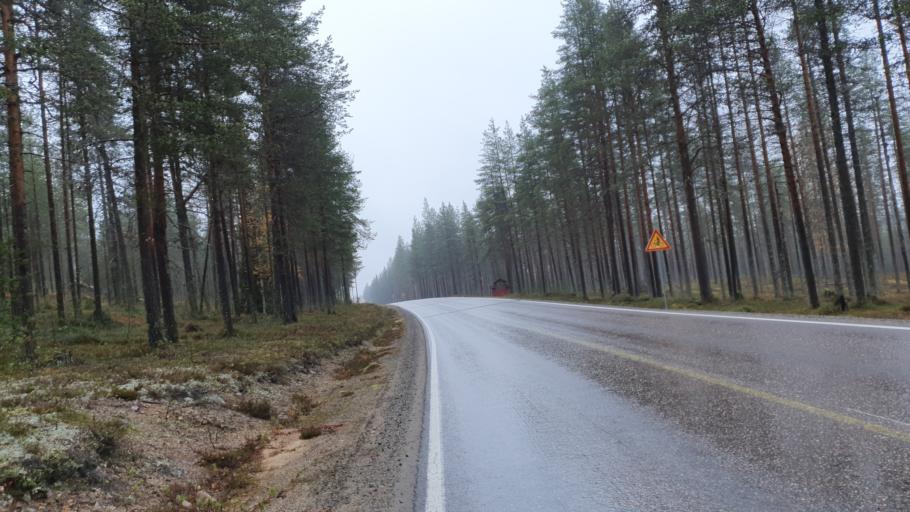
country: FI
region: Lapland
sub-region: Tunturi-Lappi
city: Kolari
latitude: 67.5957
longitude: 24.1159
